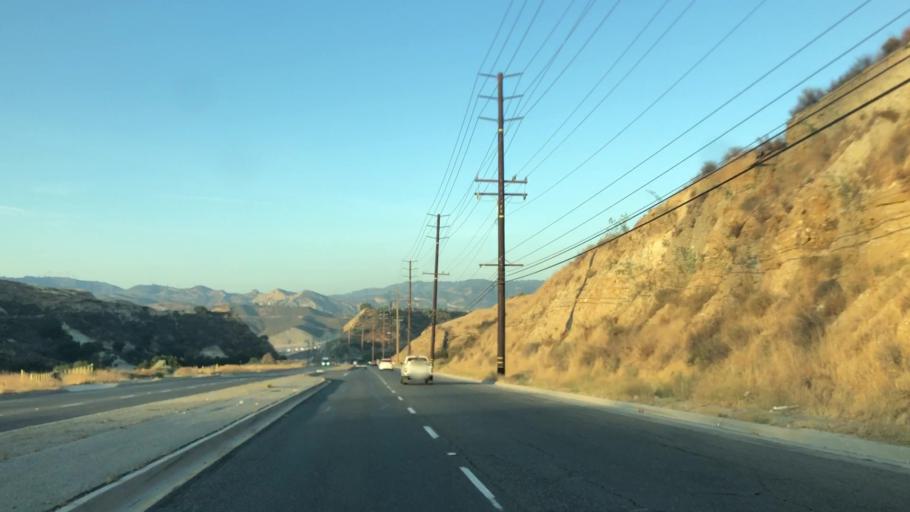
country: US
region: California
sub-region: Los Angeles County
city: Santa Clarita
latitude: 34.3919
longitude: -118.4879
